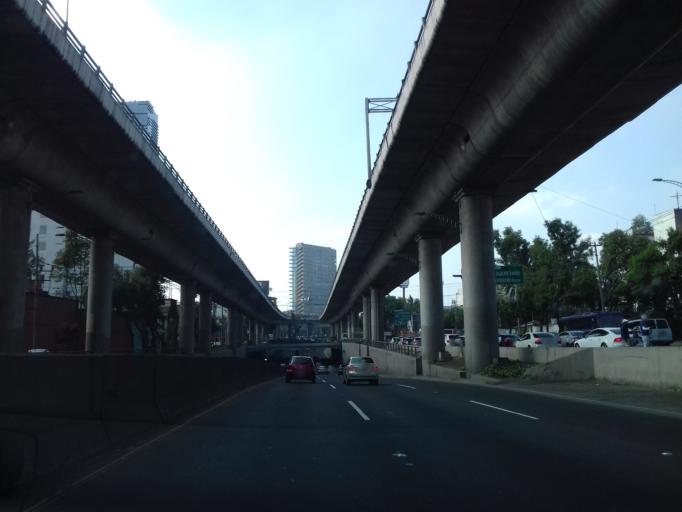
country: MX
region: Mexico City
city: Alvaro Obregon
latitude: 19.3653
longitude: -99.1909
